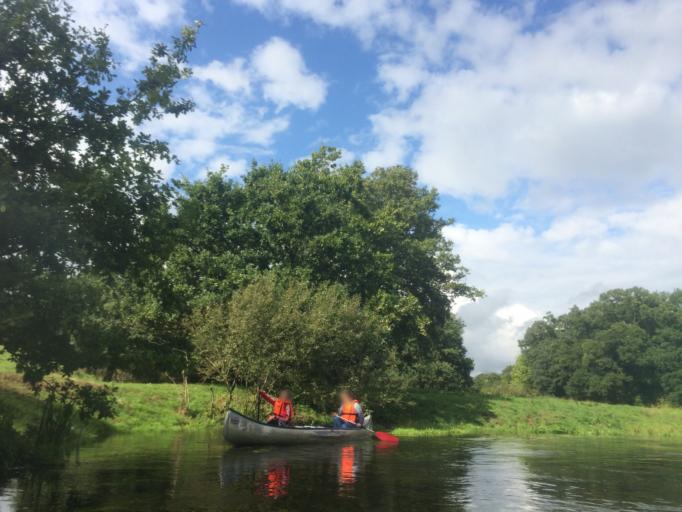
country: DK
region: South Denmark
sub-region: Vejle Kommune
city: Egtved
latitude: 55.6514
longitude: 9.3094
